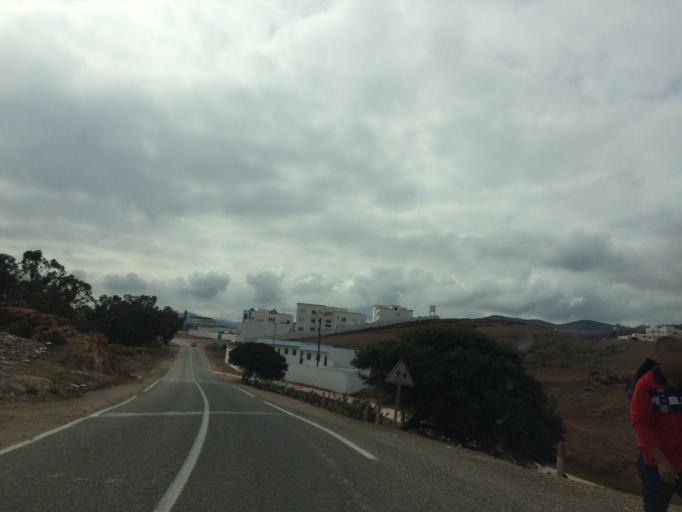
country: ES
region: Ceuta
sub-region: Ceuta
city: Ceuta
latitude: 35.8684
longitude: -5.3546
